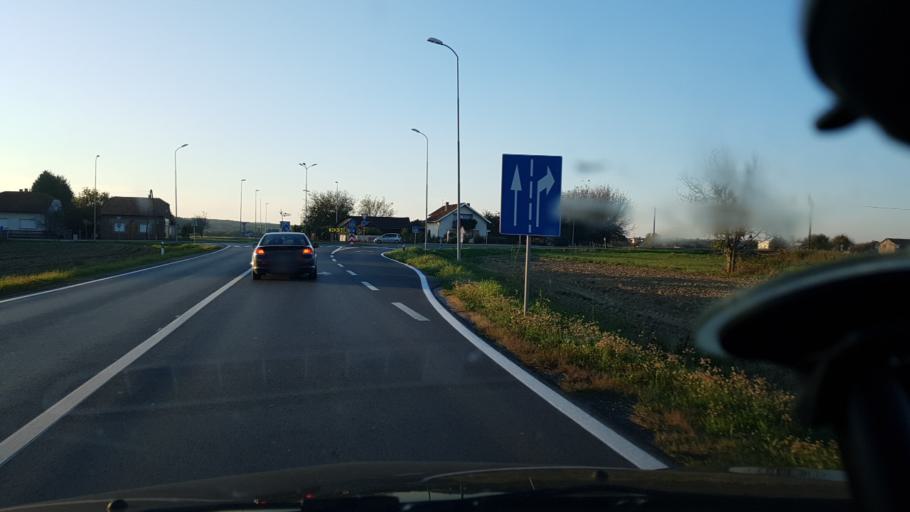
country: HR
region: Koprivnicko-Krizevacka
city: Stari Grad
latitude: 46.1474
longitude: 16.8181
